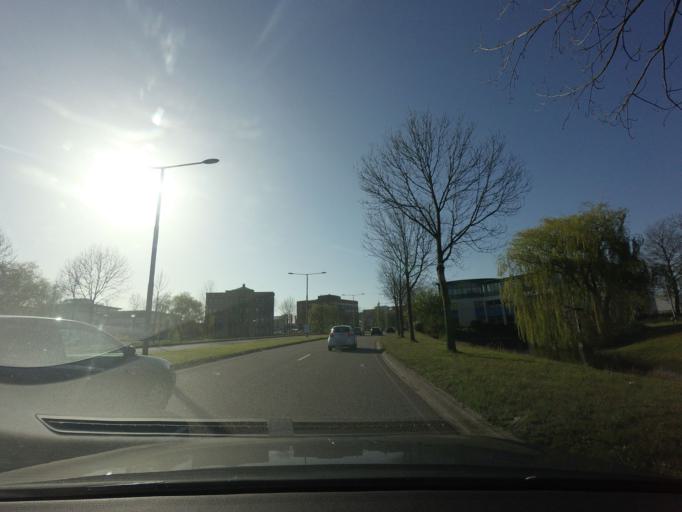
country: NL
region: Utrecht
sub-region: Gemeente Amersfoort
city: Randenbroek
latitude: 52.1732
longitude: 5.4151
